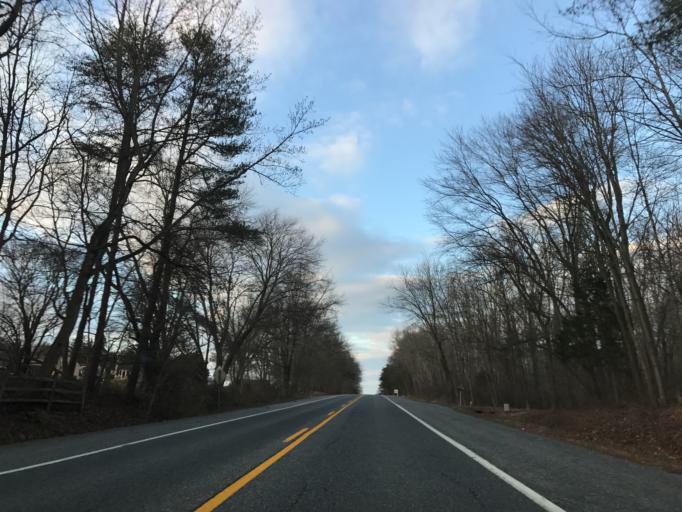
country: US
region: Maryland
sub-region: Cecil County
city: Charlestown
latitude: 39.5234
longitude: -75.9540
